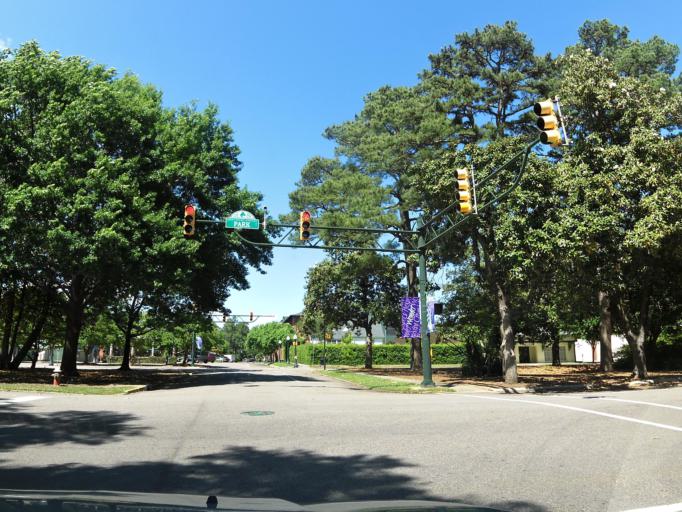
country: US
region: South Carolina
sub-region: Aiken County
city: Aiken
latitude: 33.5588
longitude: -81.7215
